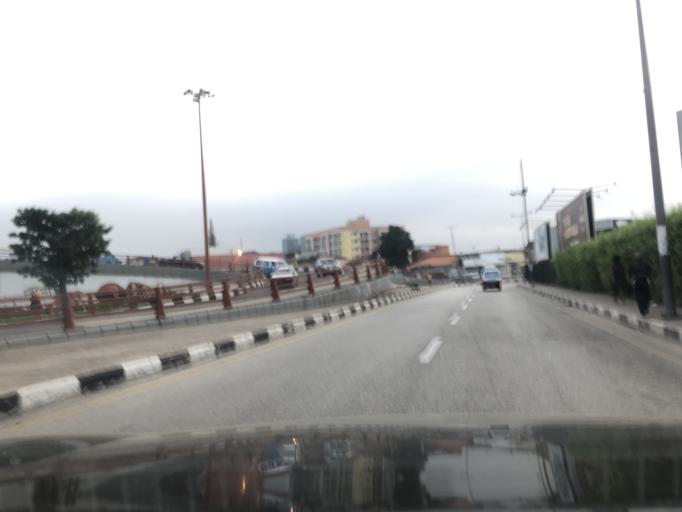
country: AO
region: Luanda
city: Luanda
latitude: -8.8462
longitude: 13.2344
